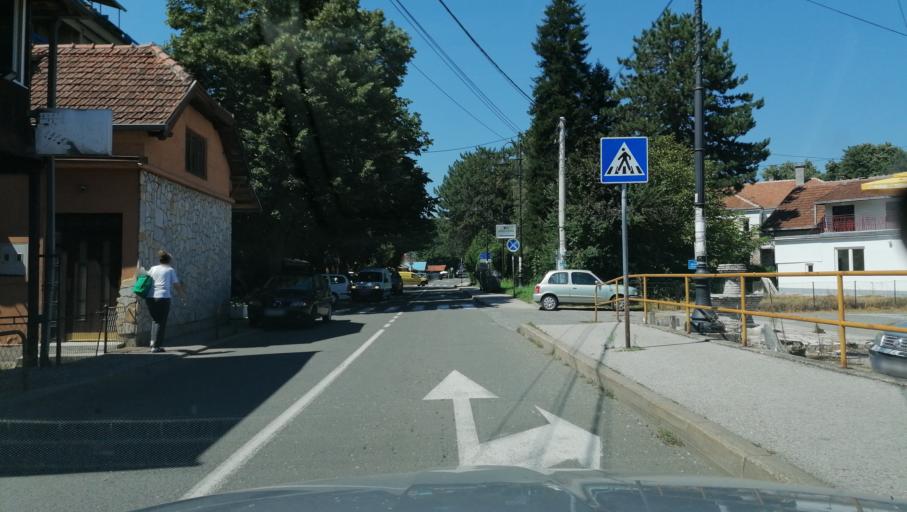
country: RS
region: Central Serbia
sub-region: Raski Okrug
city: Kraljevo
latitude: 43.6887
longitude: 20.6150
